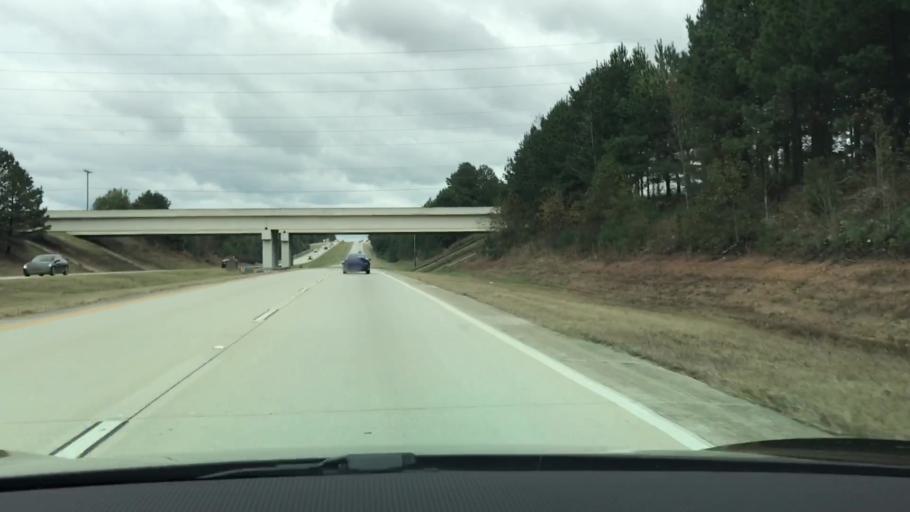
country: US
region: Georgia
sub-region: Oconee County
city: Bogart
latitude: 33.9250
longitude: -83.5137
